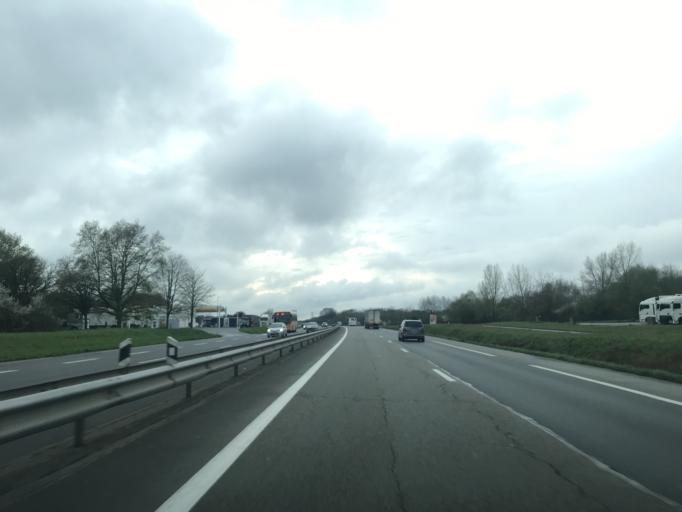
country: FR
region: Centre
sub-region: Departement du Loiret
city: Mardie
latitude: 47.9071
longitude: 2.0610
